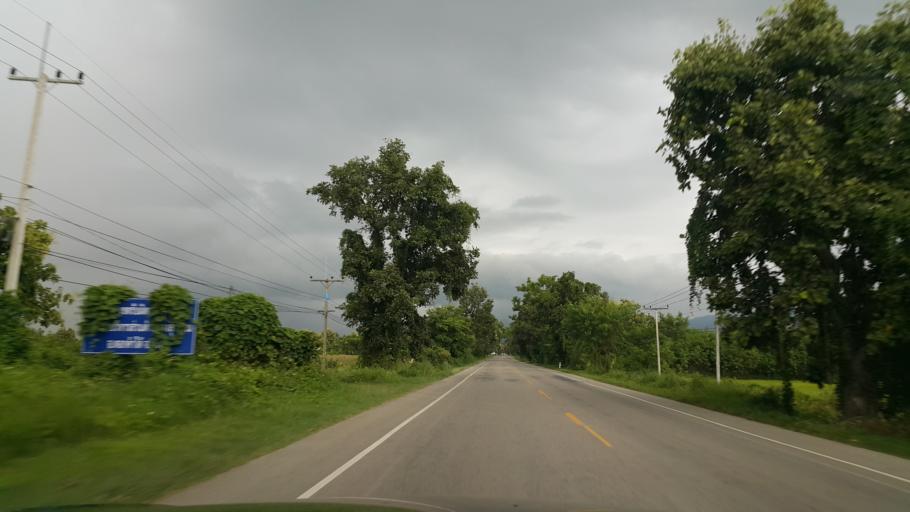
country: TH
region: Phayao
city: Dok Kham Tai
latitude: 19.2154
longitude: 100.0401
